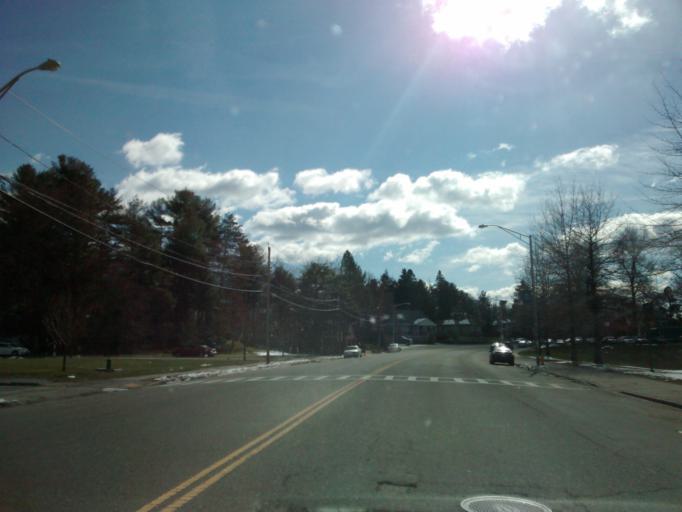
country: US
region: Massachusetts
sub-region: Worcester County
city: Worcester
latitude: 42.2702
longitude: -71.8431
